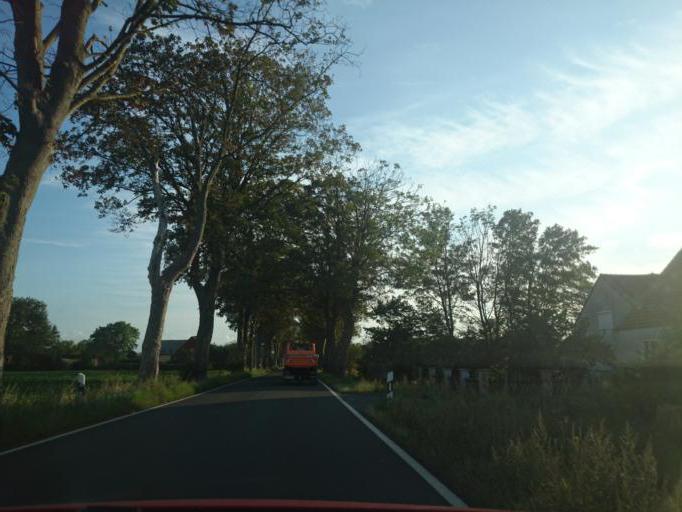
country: DE
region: Mecklenburg-Vorpommern
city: Niepars
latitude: 54.3213
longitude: 12.9356
